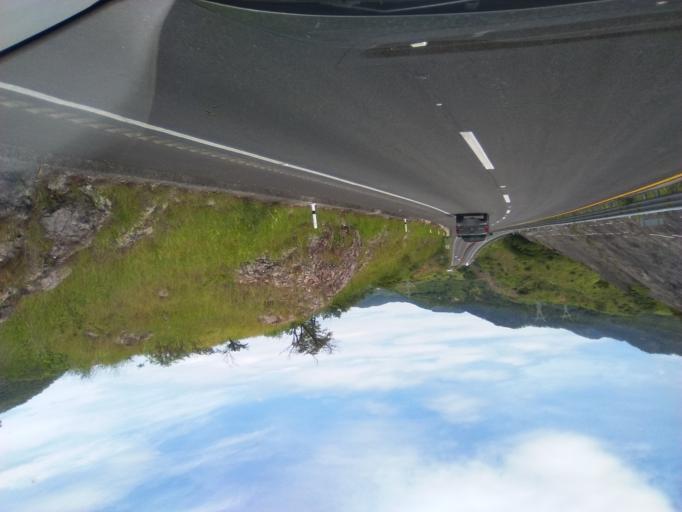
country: MX
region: Guerrero
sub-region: Chilpancingo de los Bravo
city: Acahuizotla
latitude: 17.3346
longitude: -99.4794
